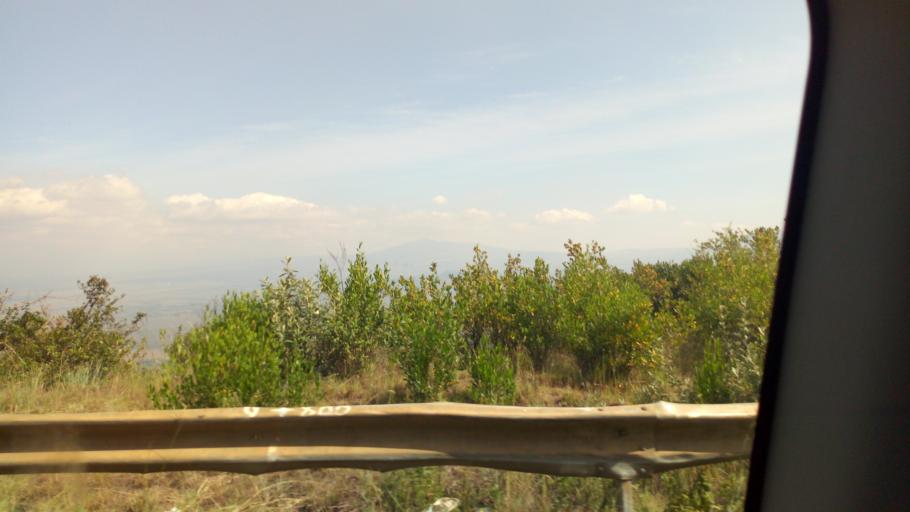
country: KE
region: Kiambu
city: Limuru
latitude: -1.0618
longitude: 36.6035
